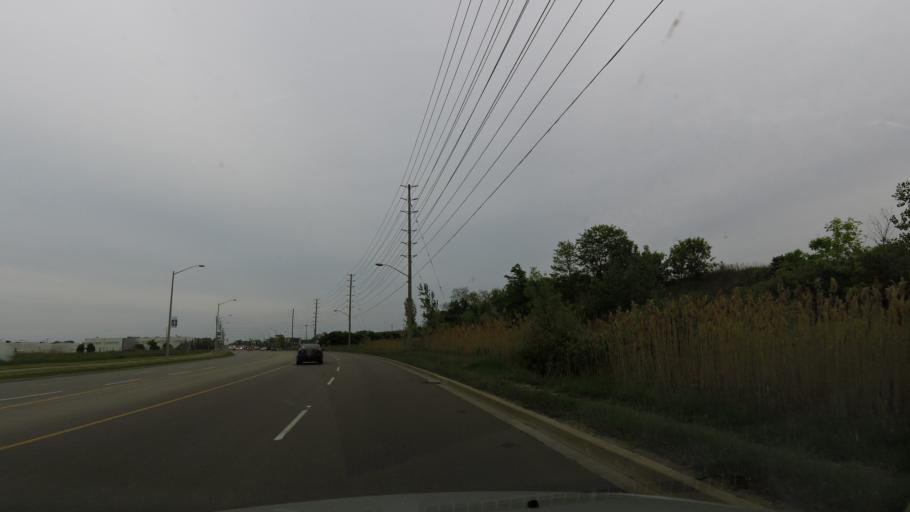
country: CA
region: Ontario
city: Ajax
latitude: 43.8693
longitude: -79.0182
